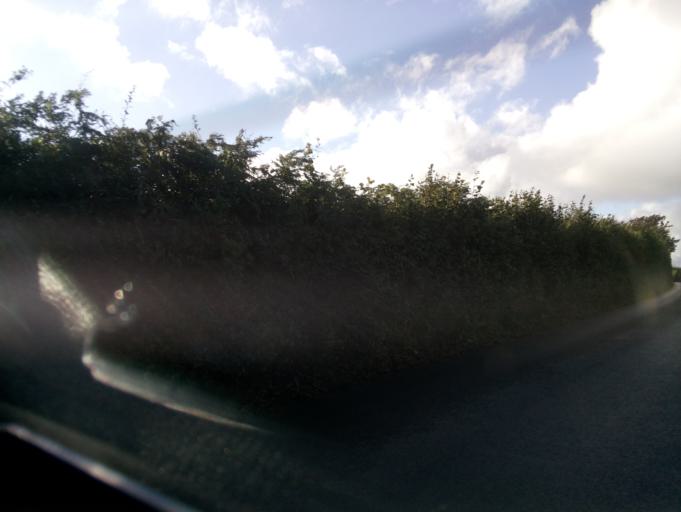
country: GB
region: England
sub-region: Devon
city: Kingsbridge
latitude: 50.3557
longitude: -3.7271
